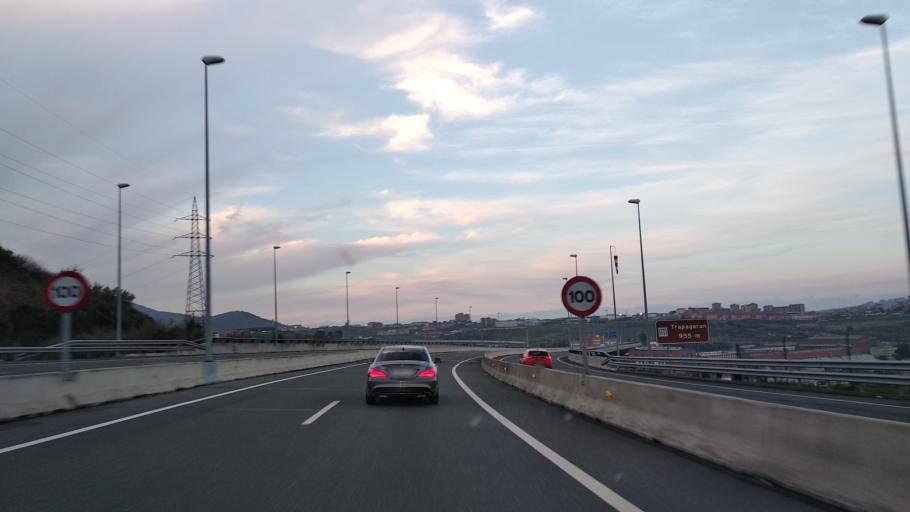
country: ES
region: Basque Country
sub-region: Bizkaia
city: Sestao
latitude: 43.2937
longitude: -3.0216
